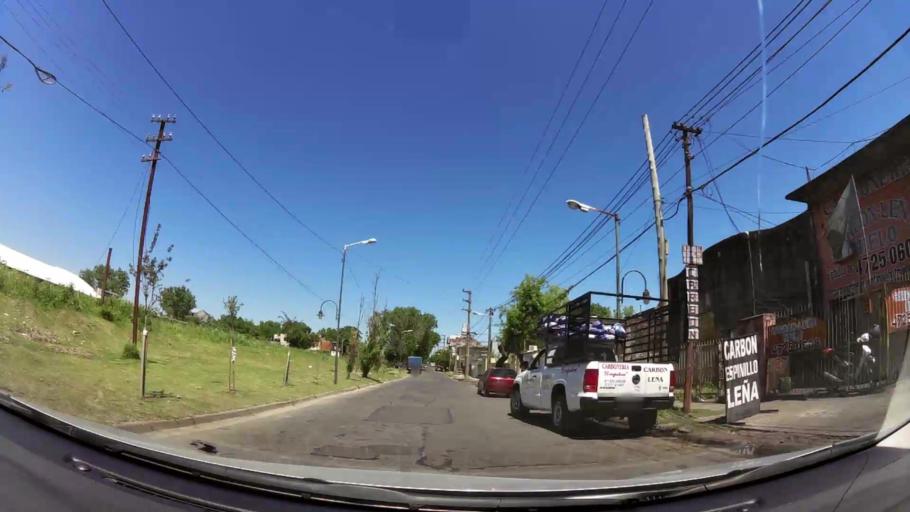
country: AR
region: Buenos Aires
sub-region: Partido de Tigre
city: Tigre
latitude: -34.4619
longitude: -58.5538
